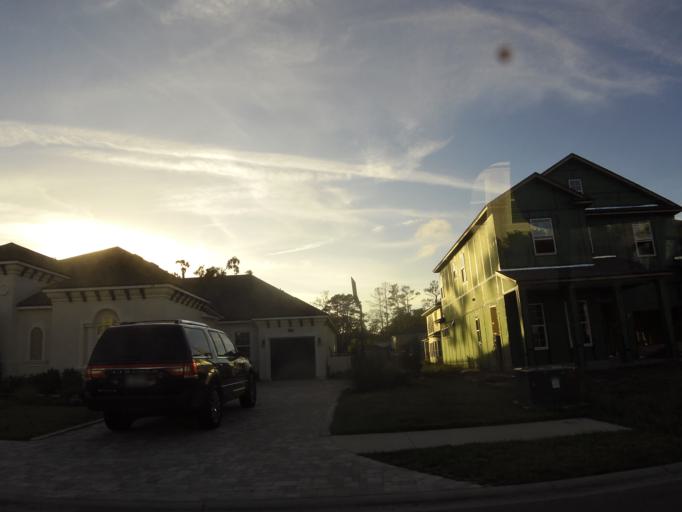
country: US
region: Florida
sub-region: Saint Johns County
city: Palm Valley
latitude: 30.1711
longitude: -81.3845
